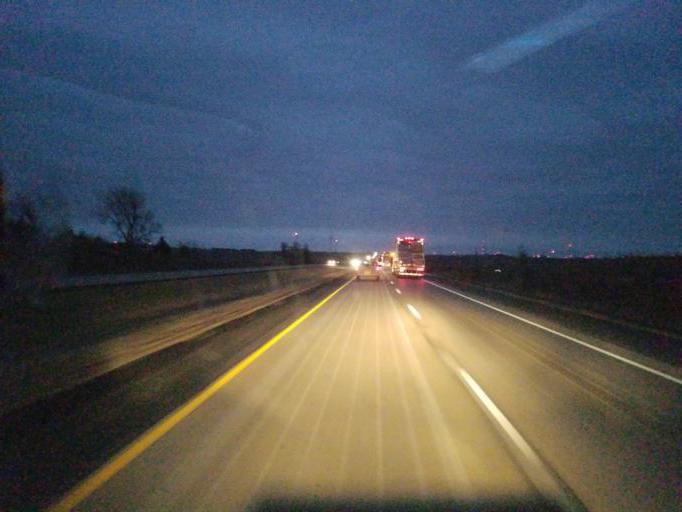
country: US
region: Iowa
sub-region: Guthrie County
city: Guthrie Center
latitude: 41.4968
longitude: -94.7282
